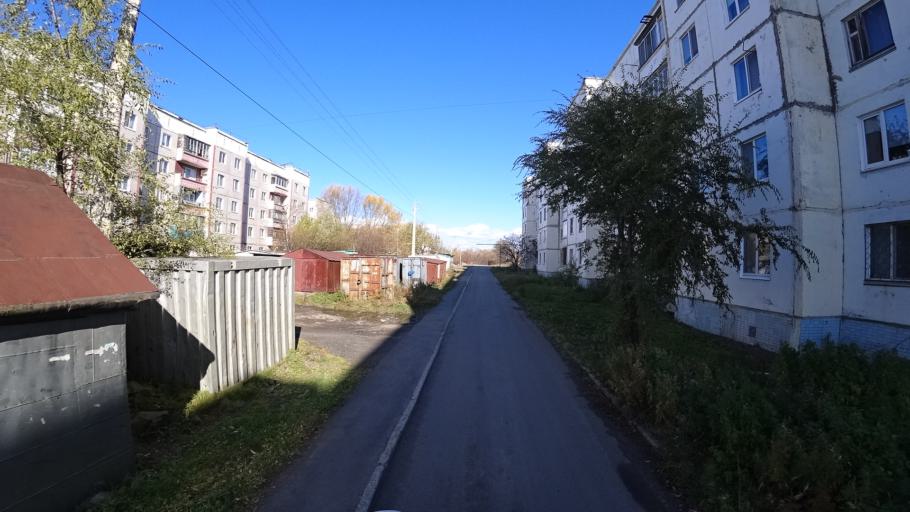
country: RU
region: Khabarovsk Krai
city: Amursk
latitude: 50.1040
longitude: 136.5166
